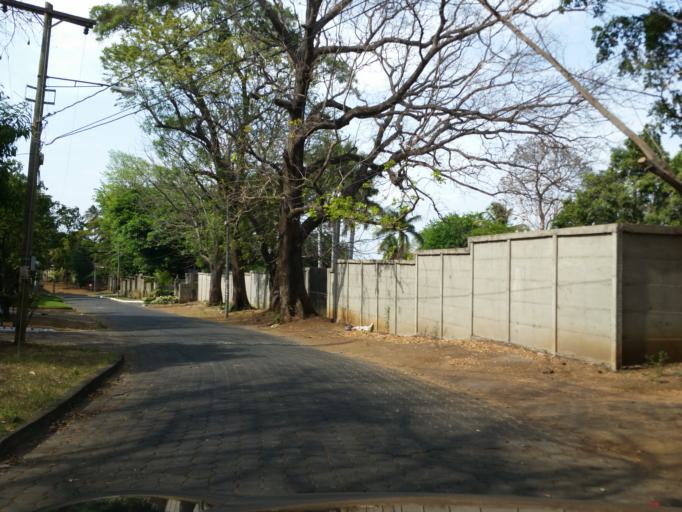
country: NI
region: Managua
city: Managua
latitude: 12.0930
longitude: -86.2298
